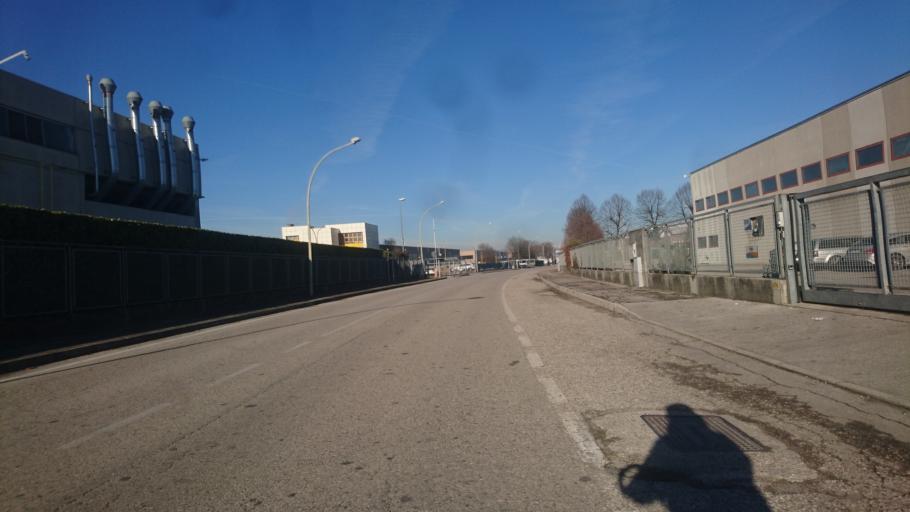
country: IT
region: Veneto
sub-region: Provincia di Padova
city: Limena
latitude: 45.4586
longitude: 11.8483
